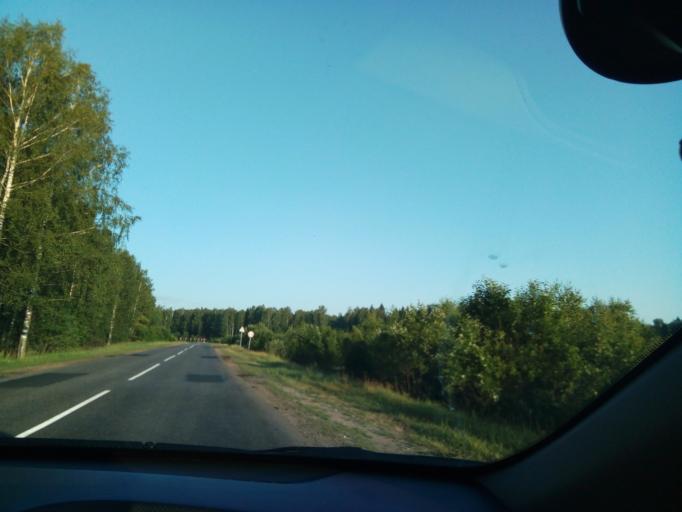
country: RU
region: Nizjnij Novgorod
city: Satis
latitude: 54.9295
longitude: 43.1997
